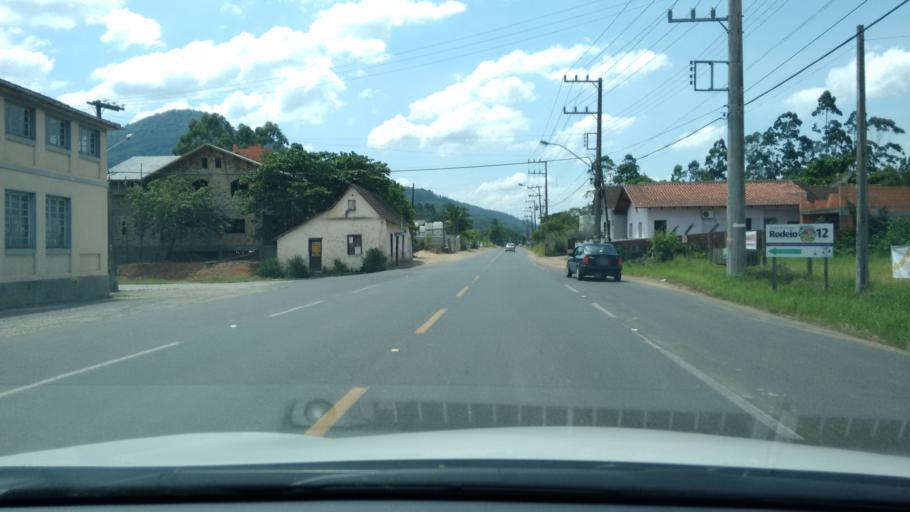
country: BR
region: Santa Catarina
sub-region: Timbo
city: Timbo
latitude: -26.8383
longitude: -49.3244
